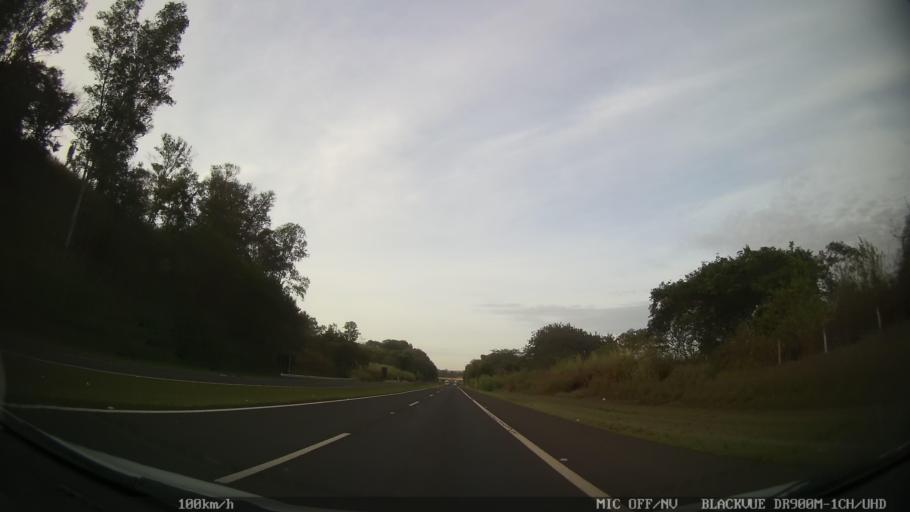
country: BR
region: Sao Paulo
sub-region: Piracicaba
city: Piracicaba
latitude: -22.6905
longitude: -47.5866
